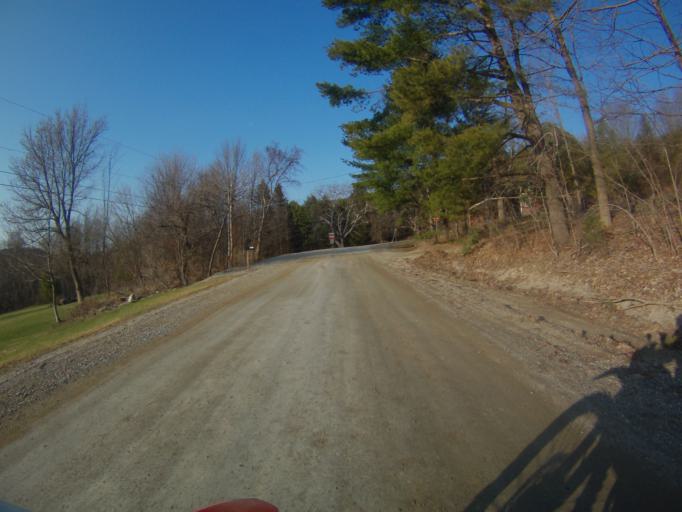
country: US
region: Vermont
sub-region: Addison County
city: Bristol
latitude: 44.1215
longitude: -73.0824
